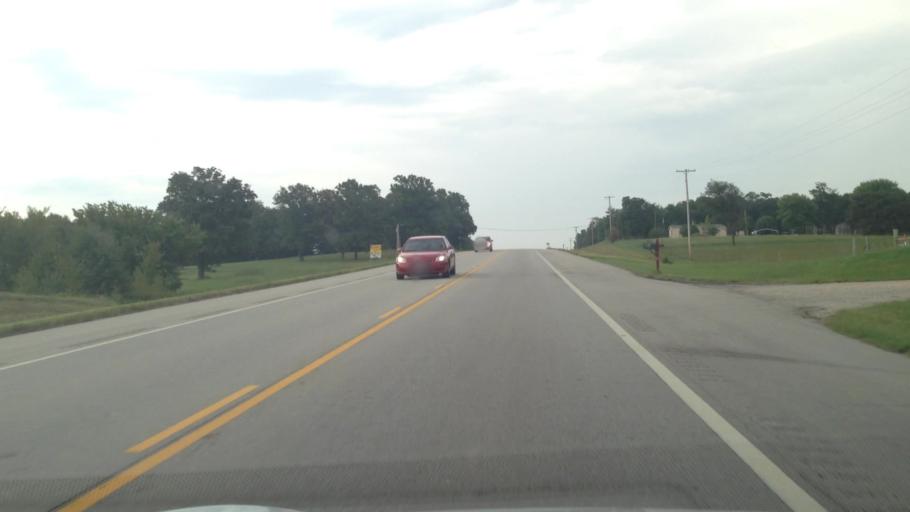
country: US
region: Kansas
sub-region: Cherokee County
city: Baxter Springs
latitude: 37.0237
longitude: -94.6847
